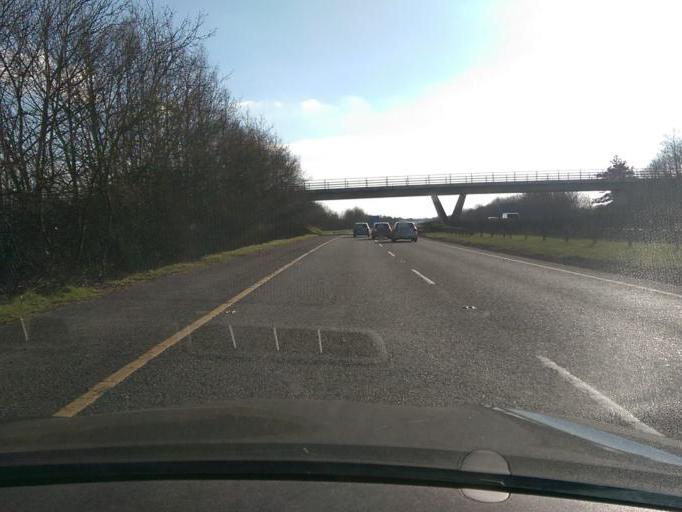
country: IE
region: Leinster
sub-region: Kildare
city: Naas
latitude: 53.1947
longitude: -6.7229
